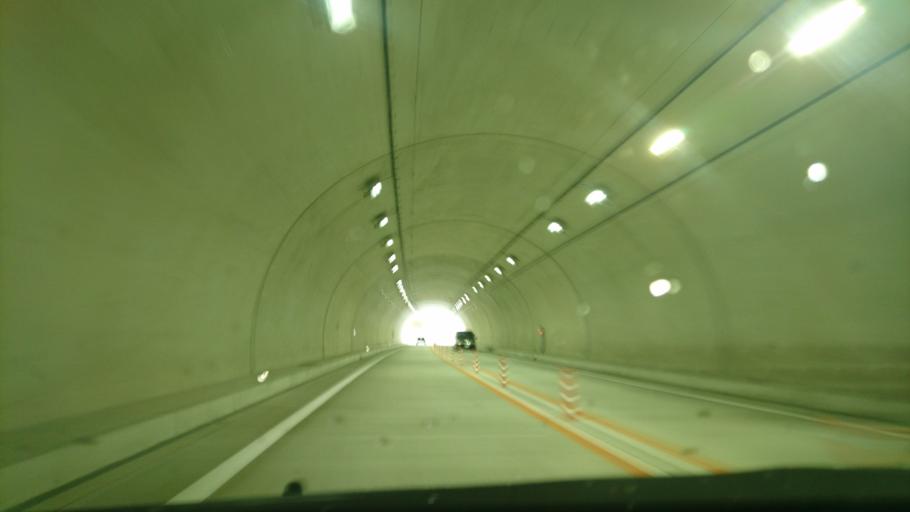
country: JP
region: Iwate
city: Kamaishi
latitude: 39.2940
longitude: 141.8651
